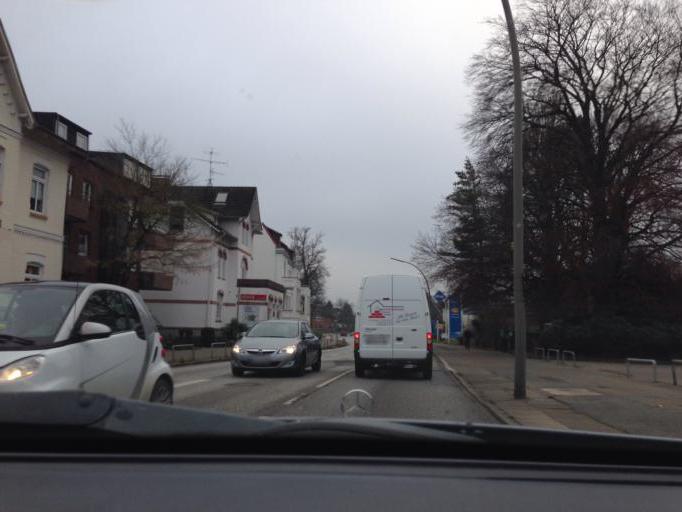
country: DE
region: Schleswig-Holstein
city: Barsbuettel
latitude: 53.5985
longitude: 10.1541
